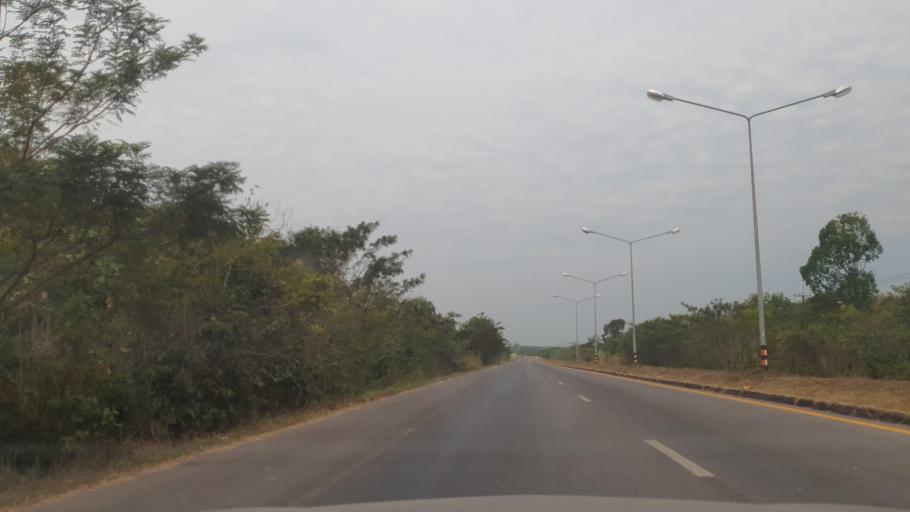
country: TH
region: Changwat Bueng Kan
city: Bung Khla
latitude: 18.2973
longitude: 103.9797
